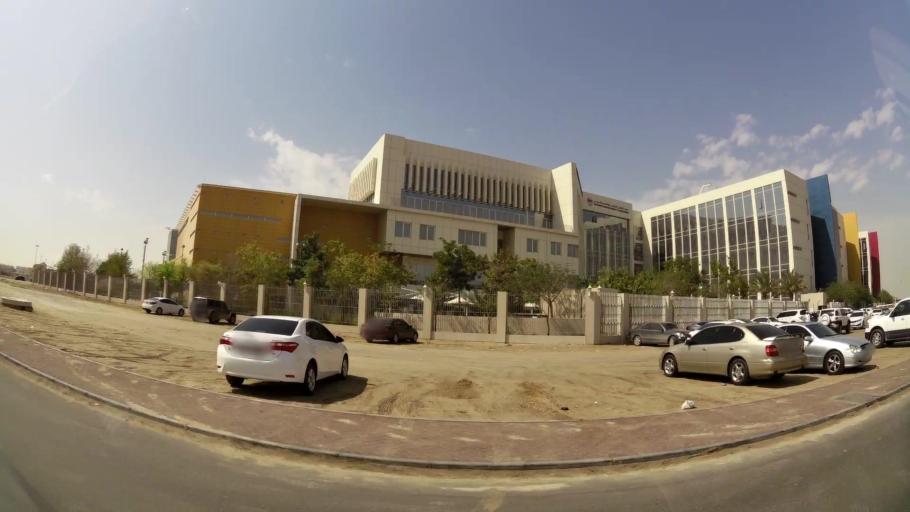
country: AE
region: Abu Dhabi
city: Abu Dhabi
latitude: 24.3136
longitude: 54.5617
